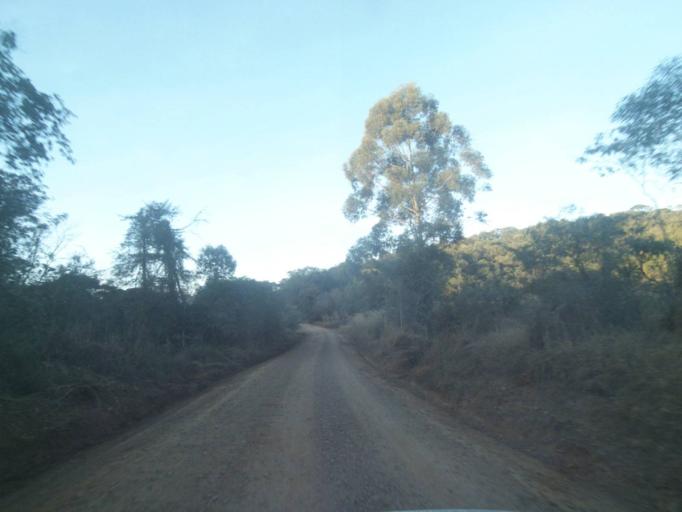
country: BR
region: Parana
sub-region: Tibagi
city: Tibagi
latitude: -24.5247
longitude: -50.5068
